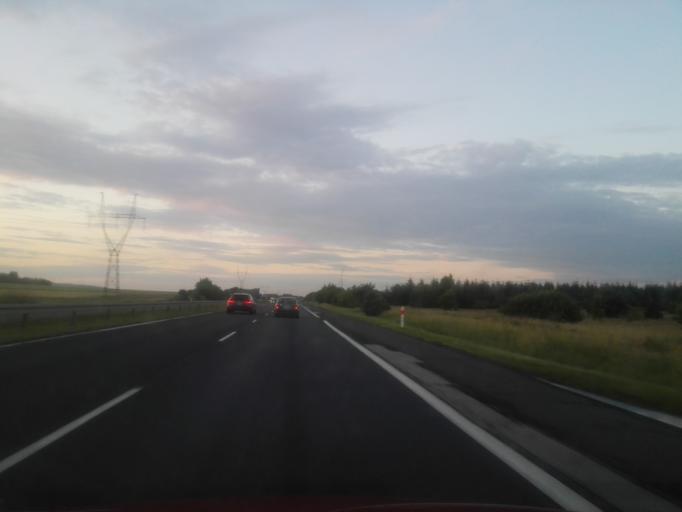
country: PL
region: Lodz Voivodeship
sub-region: Powiat radomszczanski
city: Radomsko
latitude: 51.1246
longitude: 19.4075
